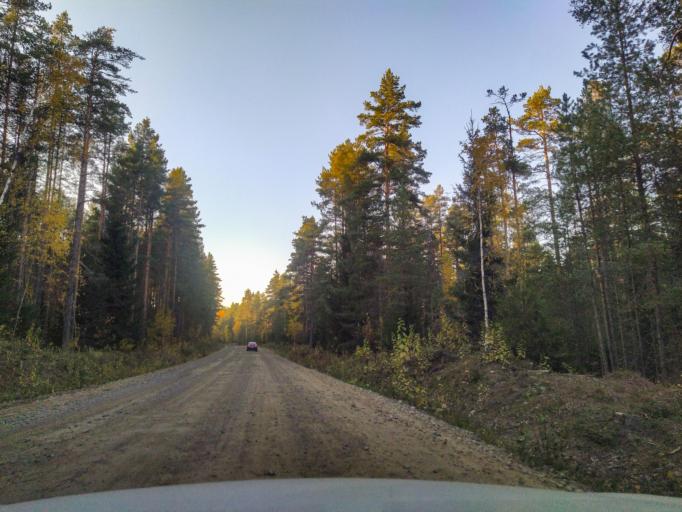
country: RU
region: Leningrad
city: Kuznechnoye
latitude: 61.3243
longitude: 29.9914
